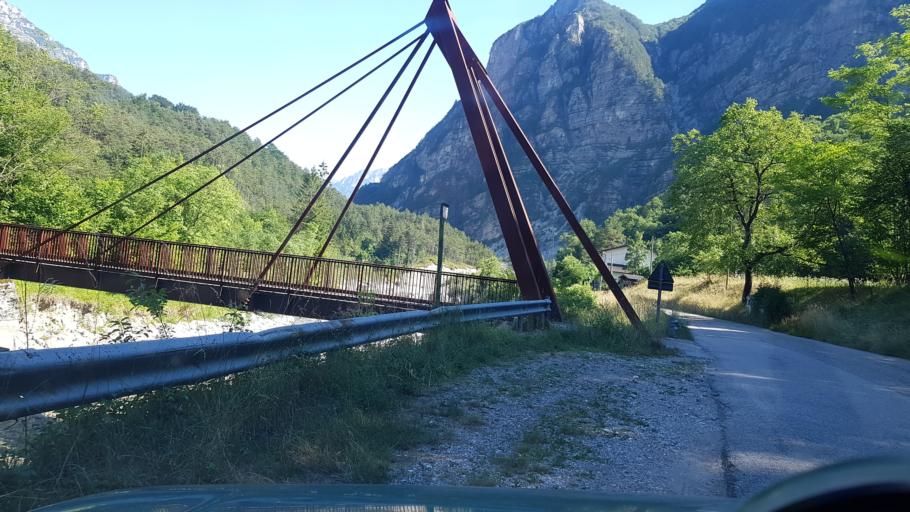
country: IT
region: Friuli Venezia Giulia
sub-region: Provincia di Udine
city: Moggio Udinese
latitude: 46.4519
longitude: 13.1874
